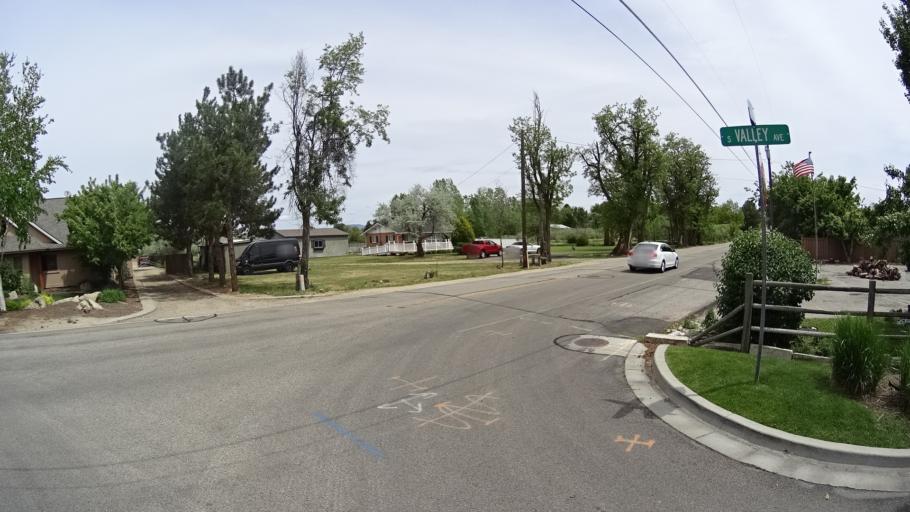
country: US
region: Idaho
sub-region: Ada County
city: Meridian
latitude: 43.5610
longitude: -116.3245
